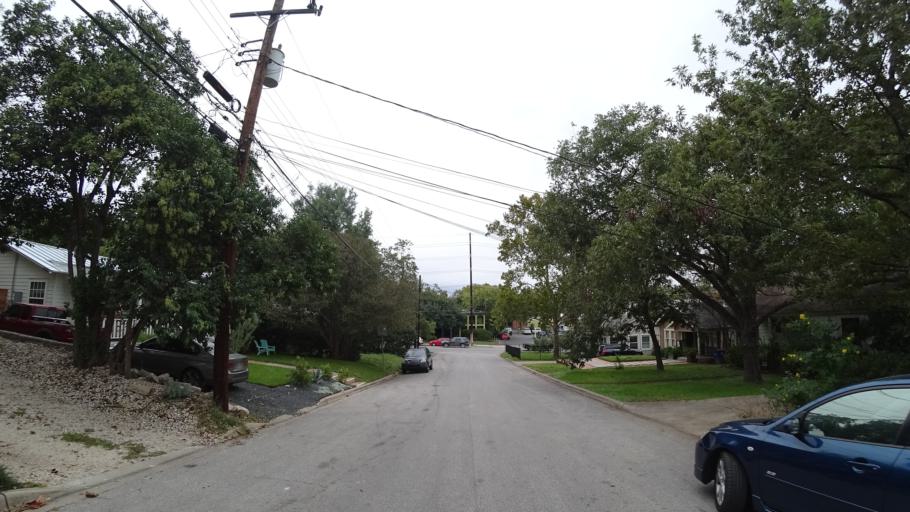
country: US
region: Texas
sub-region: Travis County
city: Austin
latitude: 30.2932
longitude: -97.7174
